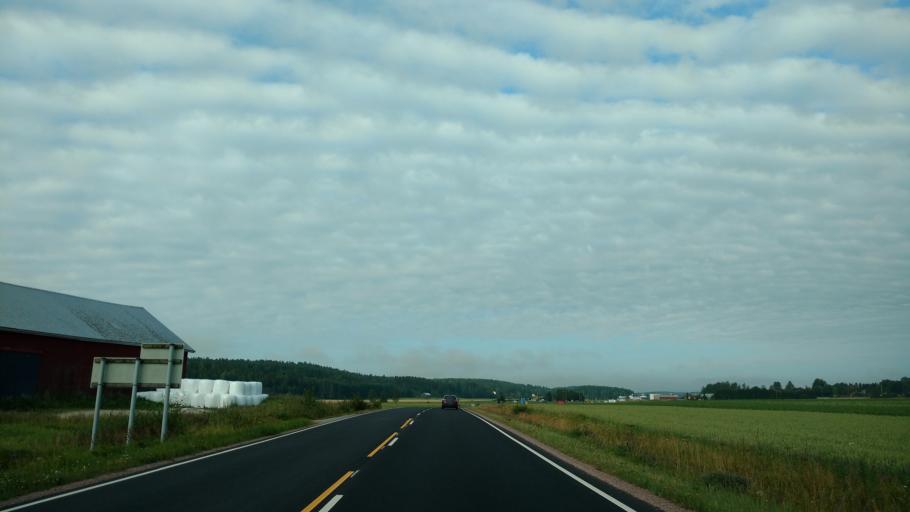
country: FI
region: Varsinais-Suomi
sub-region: Aboland-Turunmaa
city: Kimito
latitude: 60.1671
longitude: 22.7536
